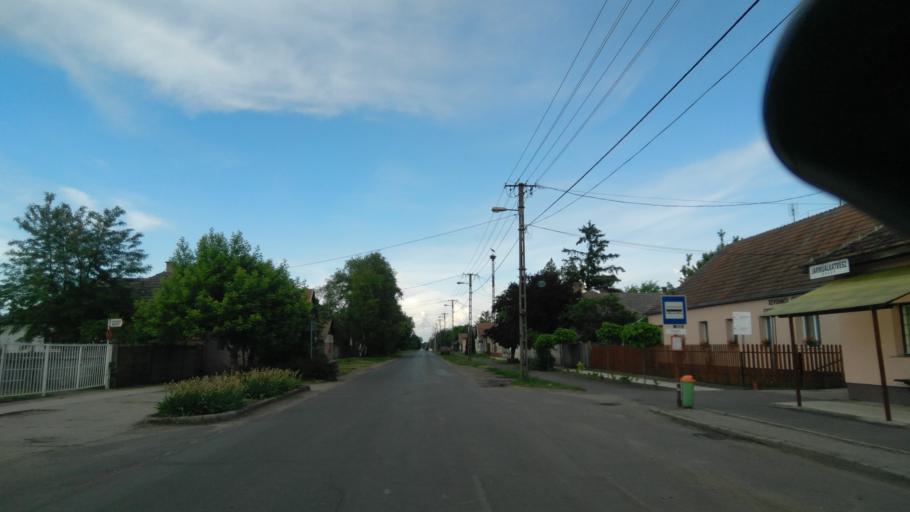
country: HU
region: Bekes
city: Kevermes
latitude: 46.4162
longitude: 21.1817
